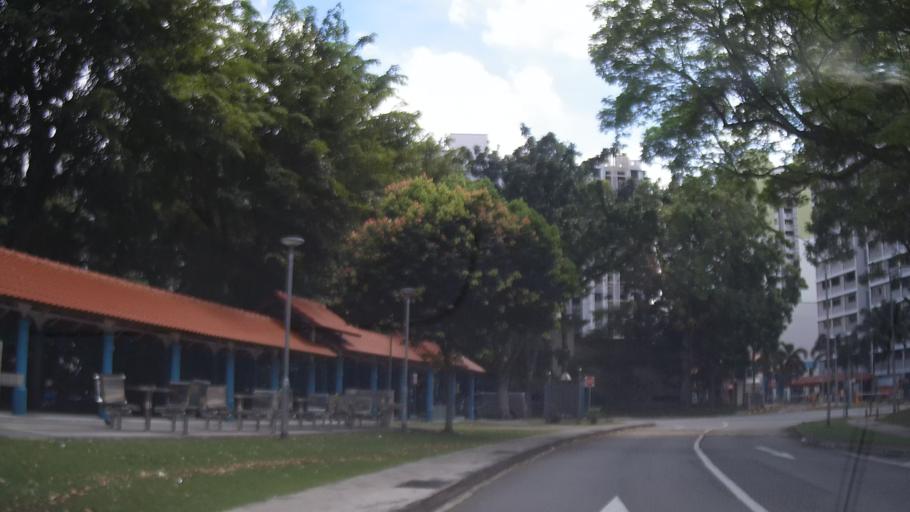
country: SG
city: Singapore
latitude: 1.3169
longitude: 103.8773
